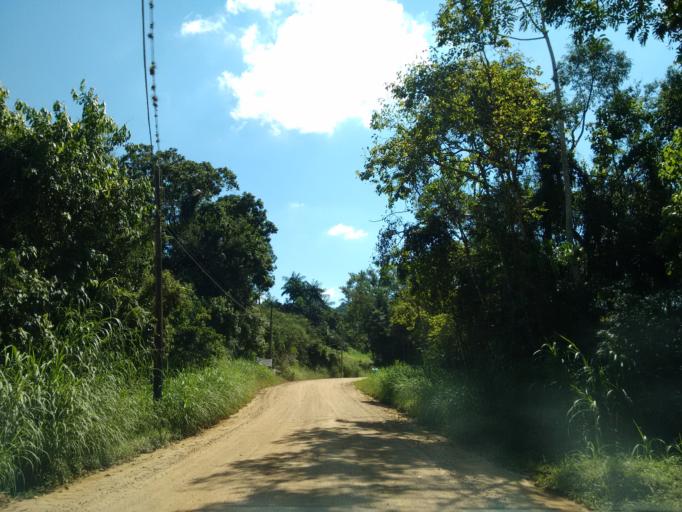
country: BR
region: Santa Catarina
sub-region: Indaial
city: Indaial
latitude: -26.9479
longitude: -49.1796
